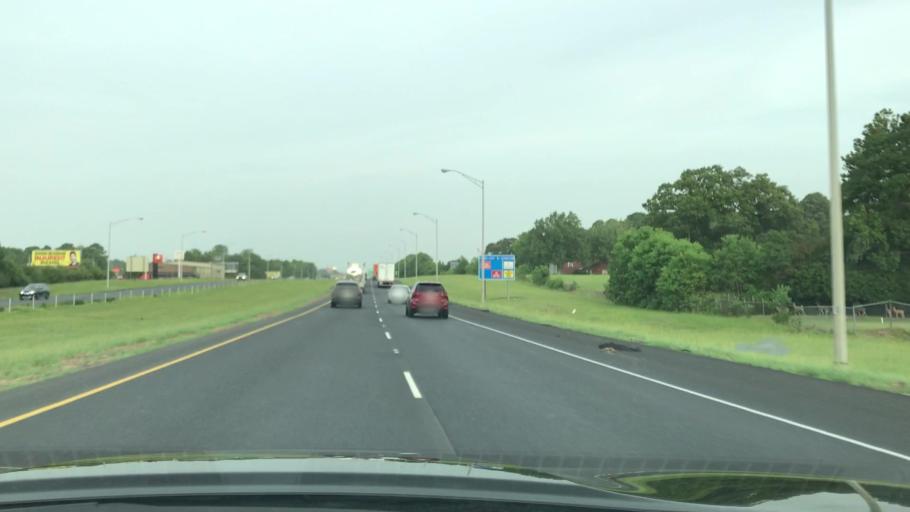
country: US
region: Louisiana
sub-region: Caddo Parish
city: Greenwood
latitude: 32.4496
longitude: -93.8877
